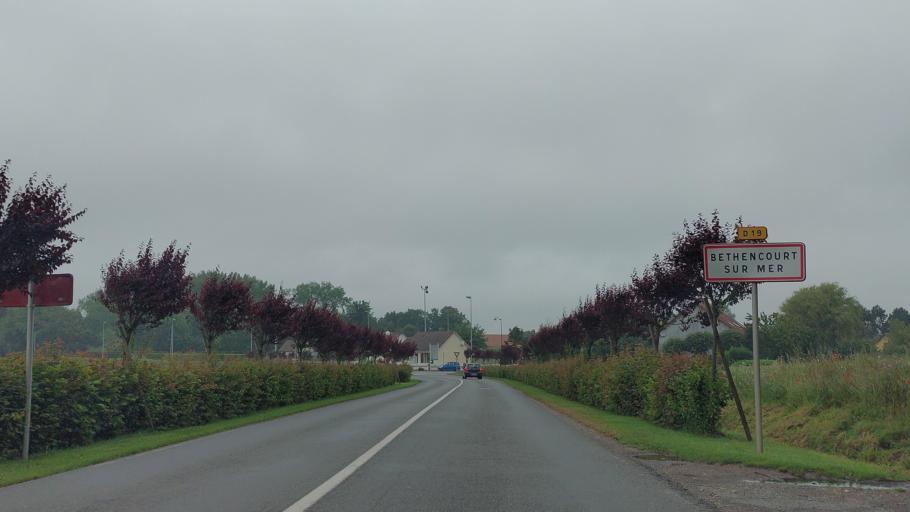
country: FR
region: Picardie
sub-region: Departement de la Somme
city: Bethencourt-sur-Mer
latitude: 50.0702
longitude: 1.5080
